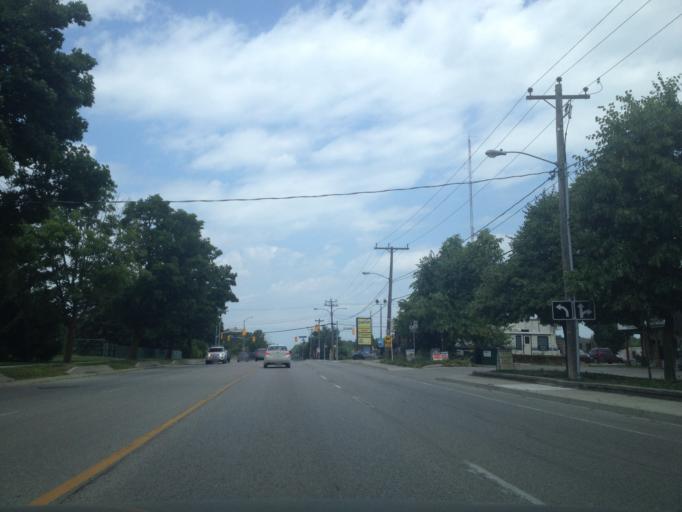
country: CA
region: Ontario
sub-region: Wellington County
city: Guelph
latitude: 43.5736
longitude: -80.2483
